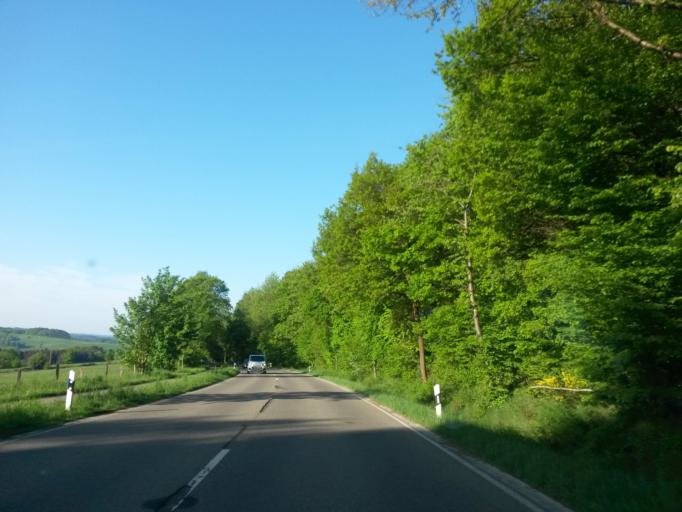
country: DE
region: North Rhine-Westphalia
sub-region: Regierungsbezirk Koln
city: Numbrecht
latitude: 50.9158
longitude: 7.4910
